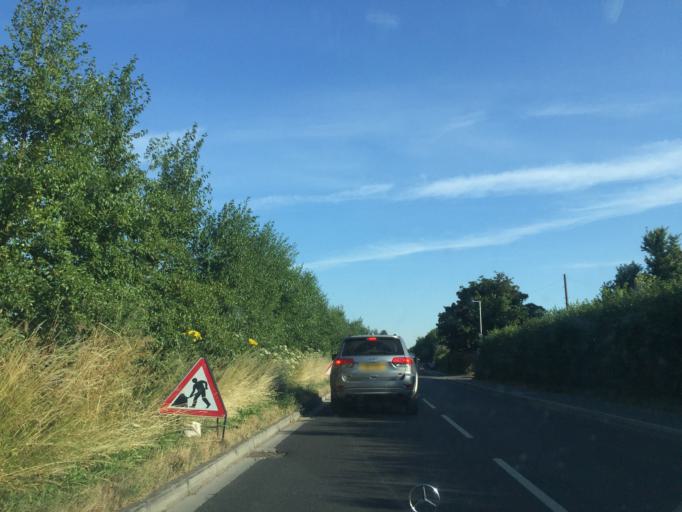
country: GB
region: England
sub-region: Wokingham
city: Wargrave
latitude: 51.4955
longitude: -0.8706
